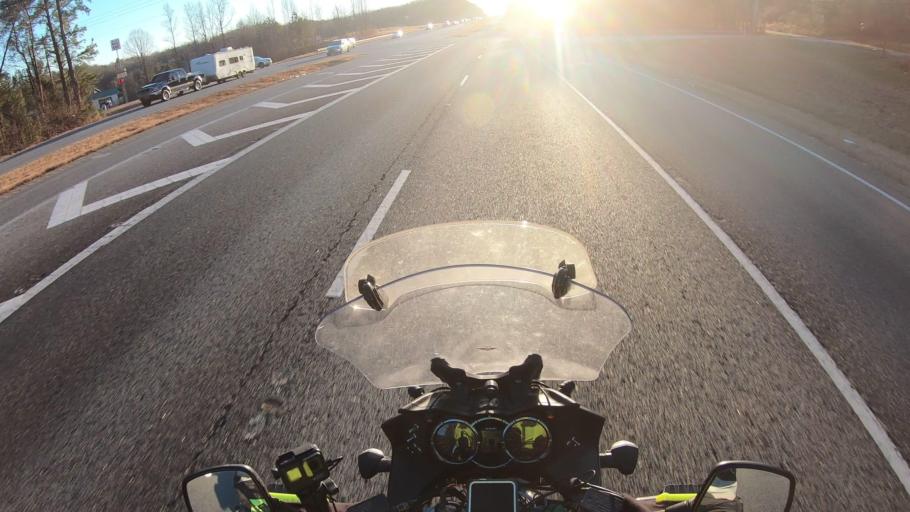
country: US
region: Georgia
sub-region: Dawson County
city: Dawsonville
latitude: 34.4047
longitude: -84.0035
